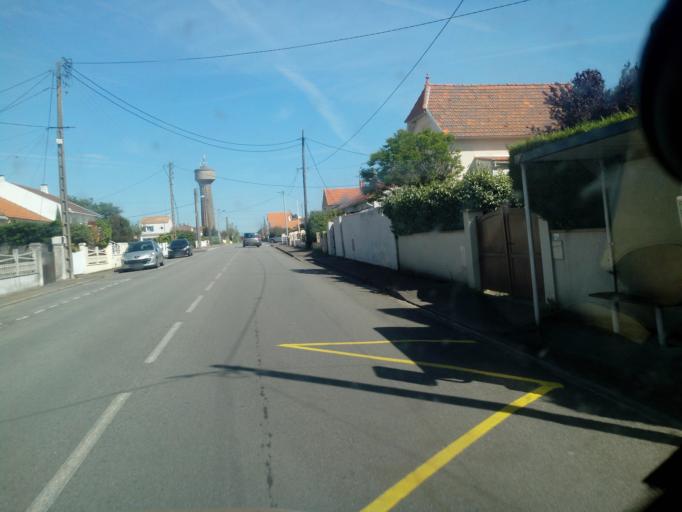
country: FR
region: Pays de la Loire
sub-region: Departement de la Loire-Atlantique
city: Pornic
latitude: 47.1094
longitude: -2.0874
